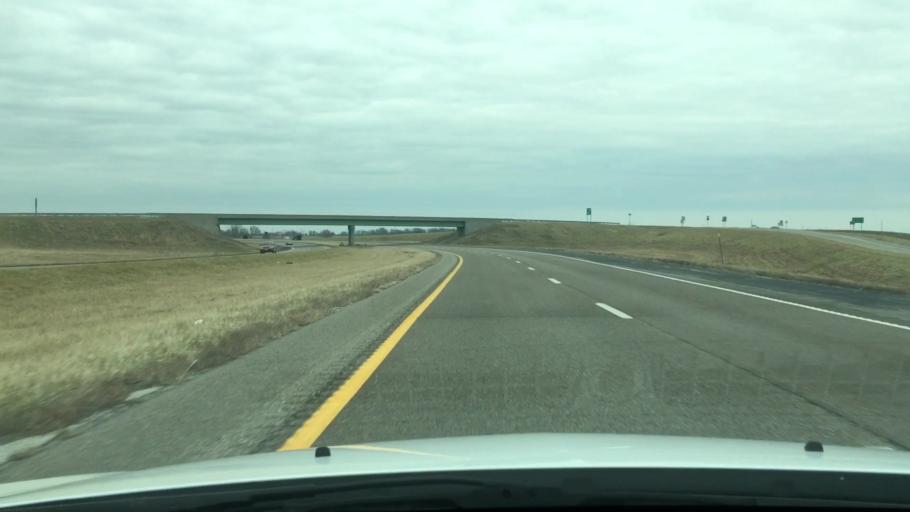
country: US
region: Missouri
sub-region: Audrain County
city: Mexico
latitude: 39.0159
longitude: -91.8875
